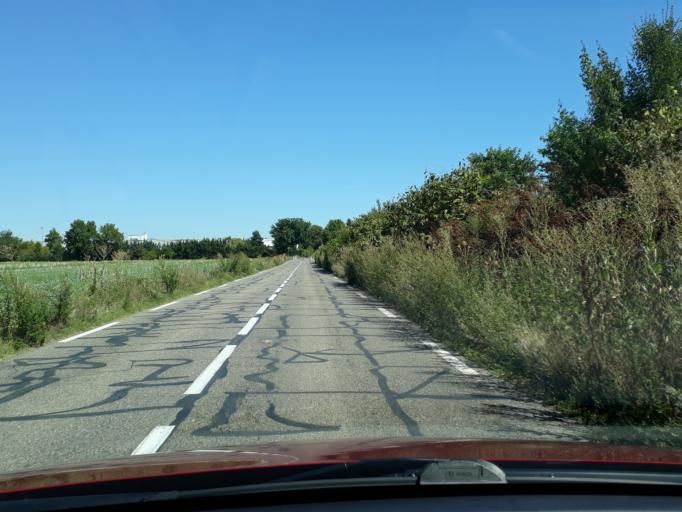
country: FR
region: Rhone-Alpes
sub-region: Departement du Rhone
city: Genas
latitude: 45.7044
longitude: 4.9843
